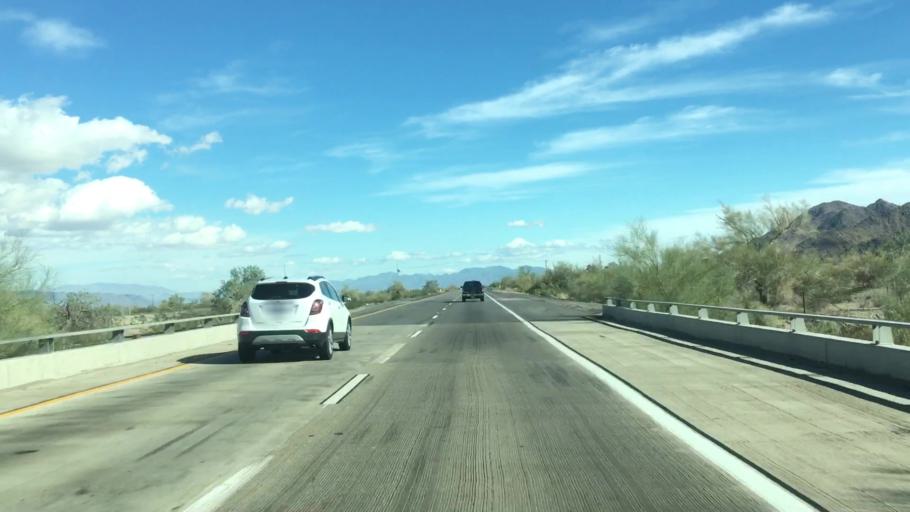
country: US
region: California
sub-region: Imperial County
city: Niland
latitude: 33.6866
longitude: -115.5228
